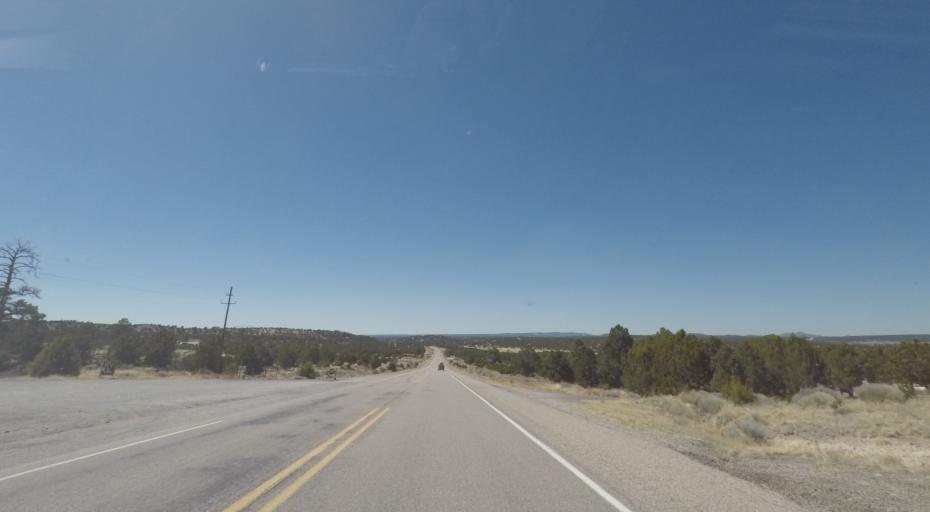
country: US
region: New Mexico
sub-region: Socorro County
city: Alamo
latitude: 34.3000
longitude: -108.1341
